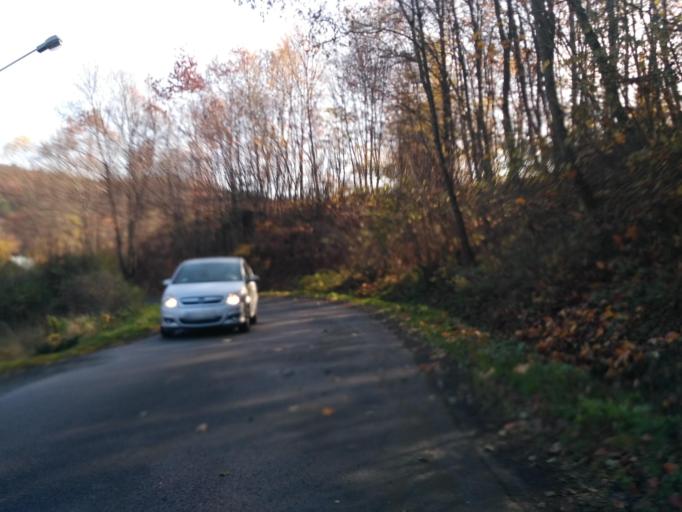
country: PL
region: Subcarpathian Voivodeship
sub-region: Powiat brzozowski
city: Nozdrzec
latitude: 49.7898
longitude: 22.2090
